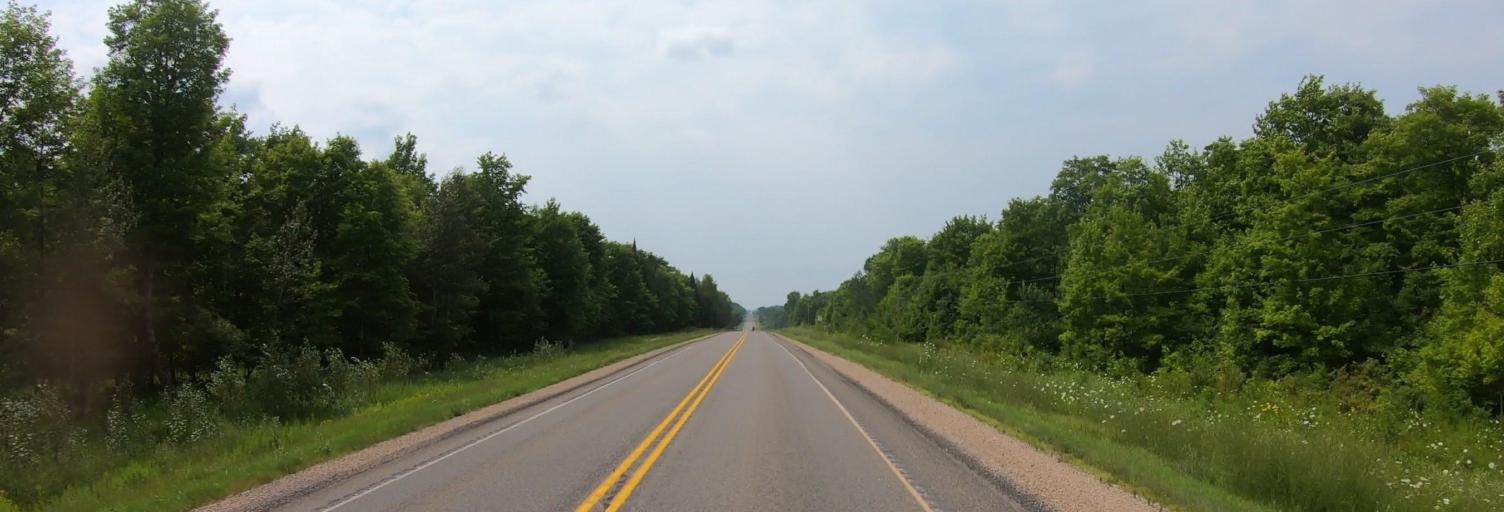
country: US
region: Michigan
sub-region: Alger County
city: Munising
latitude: 46.3329
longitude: -86.8726
